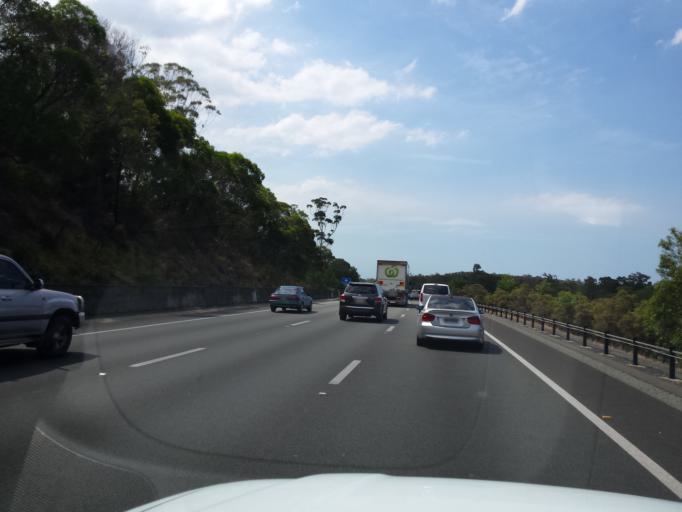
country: AU
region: Queensland
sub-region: Gold Coast
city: Nerang
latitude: -27.9711
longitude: 153.3470
